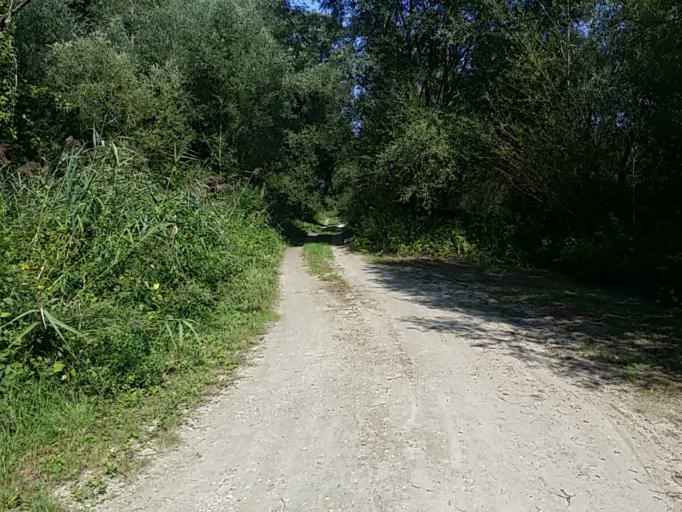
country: HR
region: Koprivnicko-Krizevacka
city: Ferdinandovac
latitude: 46.1147
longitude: 17.2102
